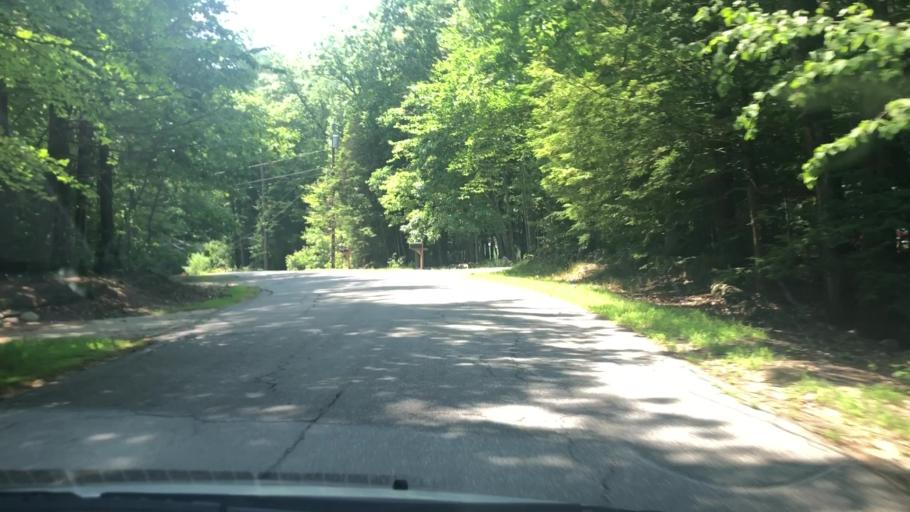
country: US
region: New Hampshire
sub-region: Hillsborough County
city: Milford
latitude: 42.8743
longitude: -71.6175
